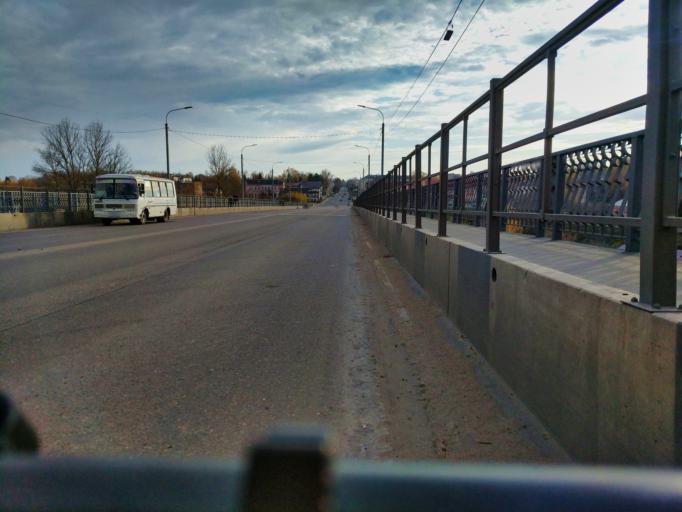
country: RU
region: Tverskaya
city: Rzhev
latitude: 56.2610
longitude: 34.3287
